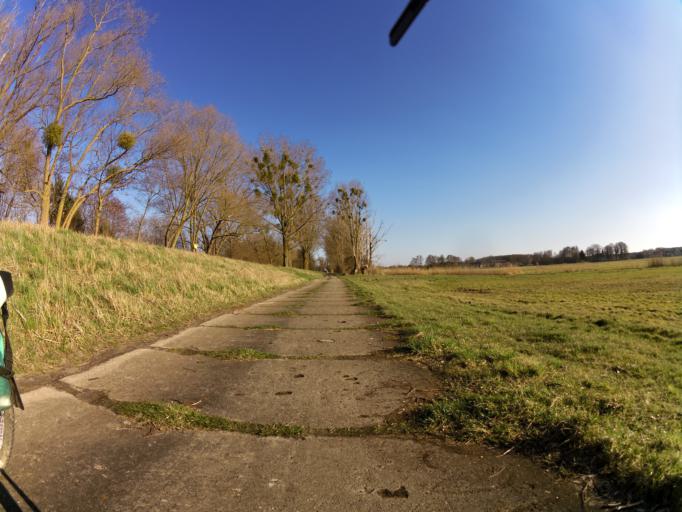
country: PL
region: West Pomeranian Voivodeship
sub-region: Powiat policki
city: Nowe Warpno
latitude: 53.7013
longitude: 14.3634
